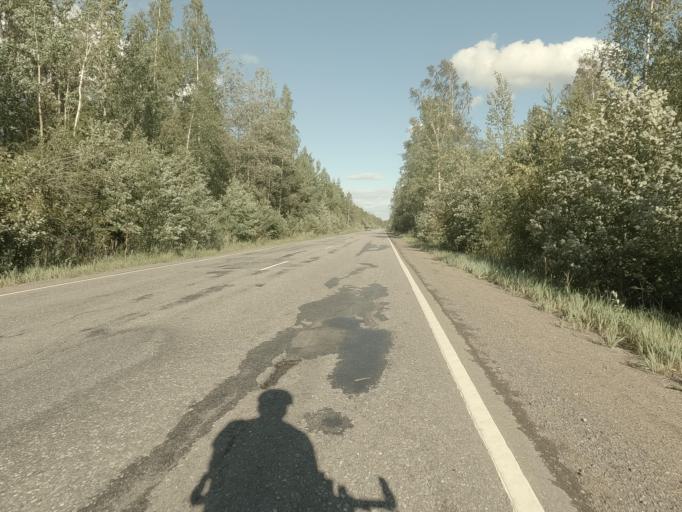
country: RU
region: Leningrad
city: Borisova Griva
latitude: 59.9852
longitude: 30.9059
